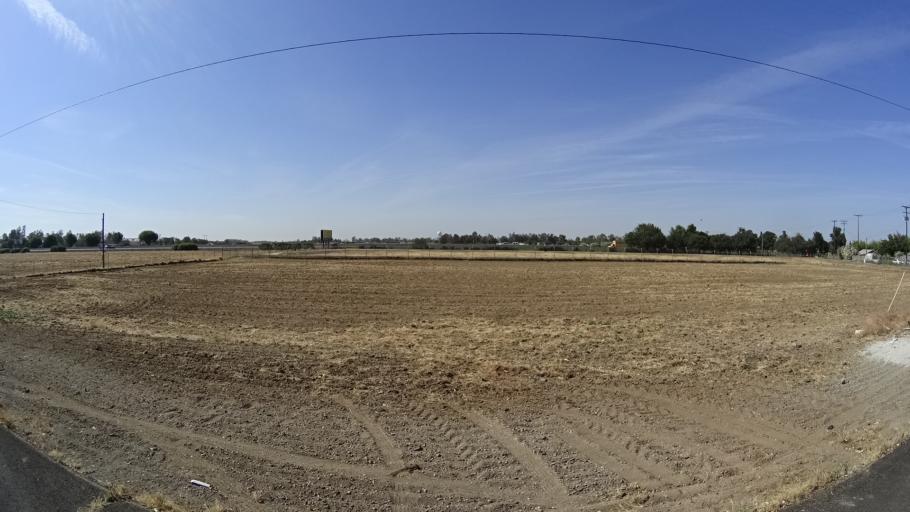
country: US
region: California
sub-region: Kings County
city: Hanford
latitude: 36.3258
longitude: -119.6329
